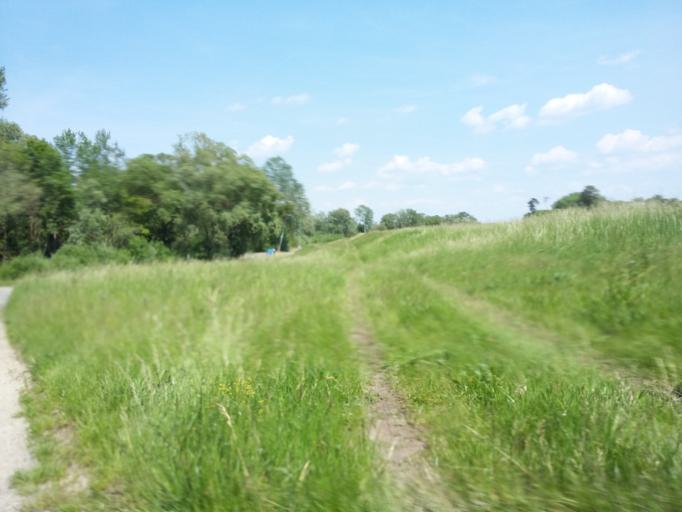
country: AT
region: Lower Austria
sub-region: Politischer Bezirk Ganserndorf
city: Drosing
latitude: 48.4991
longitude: 16.9368
